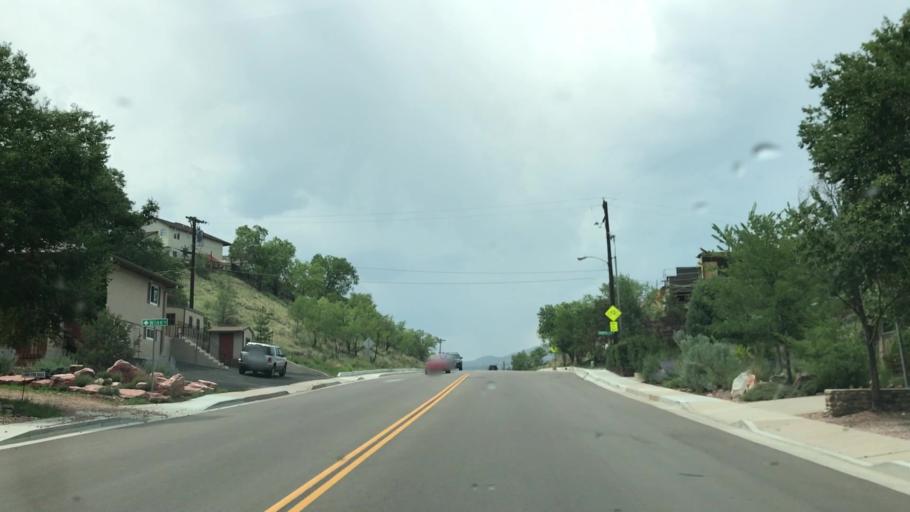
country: US
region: Colorado
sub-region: El Paso County
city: Colorado Springs
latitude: 38.8509
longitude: -104.8595
